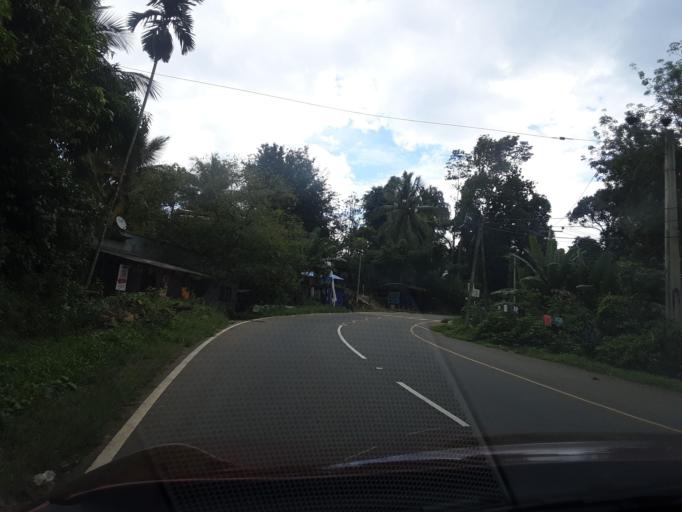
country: LK
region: Uva
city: Monaragala
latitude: 6.9034
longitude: 81.2191
